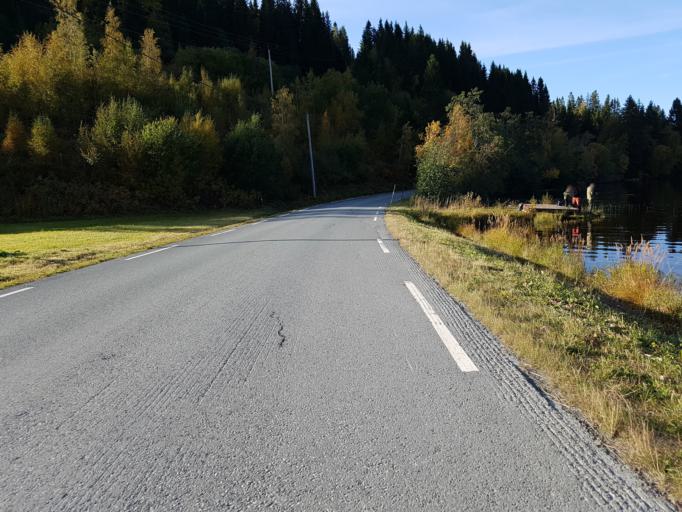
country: NO
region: Sor-Trondelag
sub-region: Klaebu
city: Klaebu
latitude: 63.3397
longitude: 10.5615
